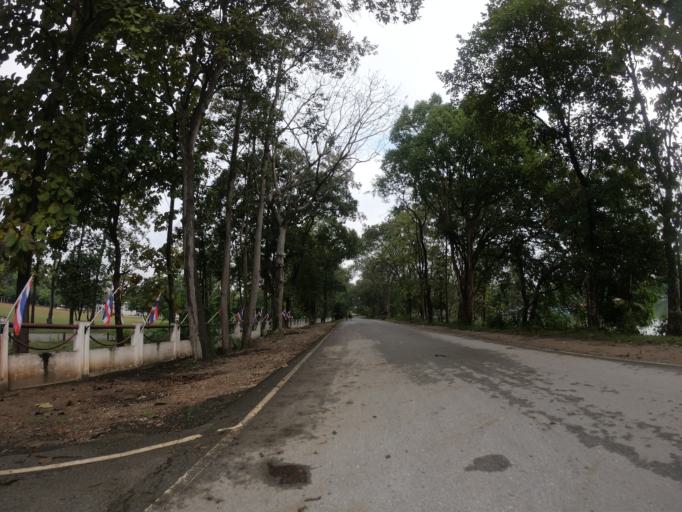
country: TH
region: Chiang Mai
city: Chiang Mai
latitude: 18.8218
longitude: 98.9736
